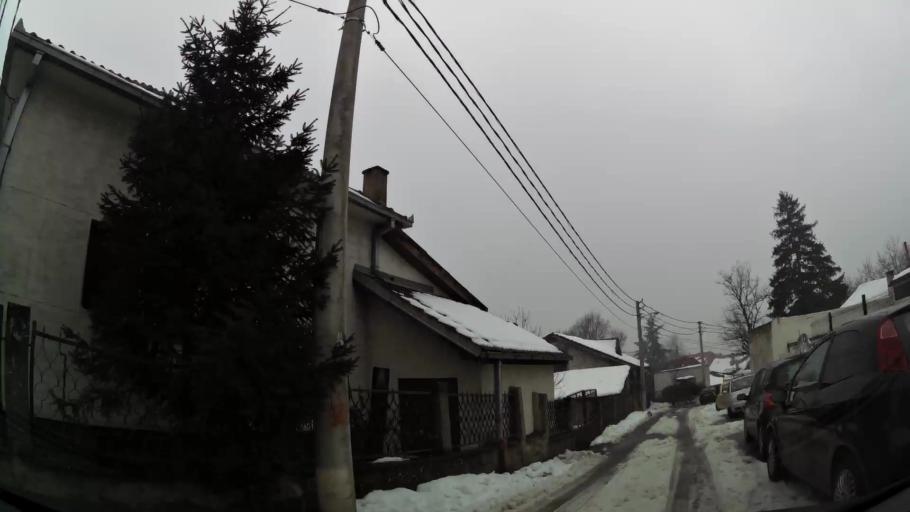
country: RS
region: Central Serbia
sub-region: Belgrade
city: Zvezdara
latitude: 44.7843
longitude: 20.5246
